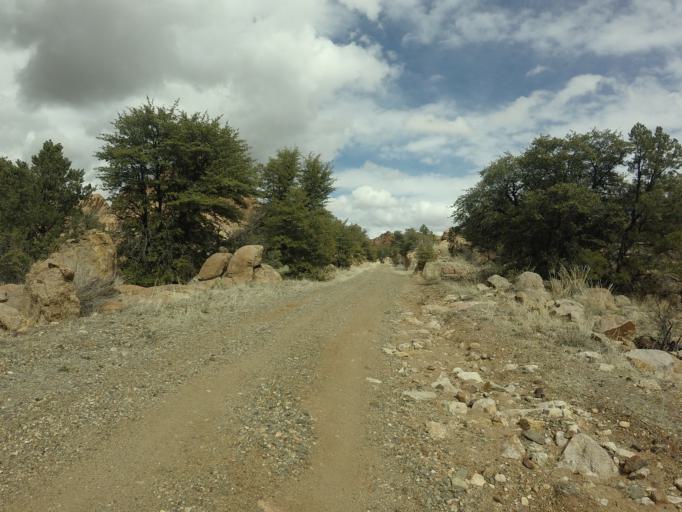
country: US
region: Arizona
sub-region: Yavapai County
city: Prescott Valley
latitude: 34.6050
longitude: -112.3917
